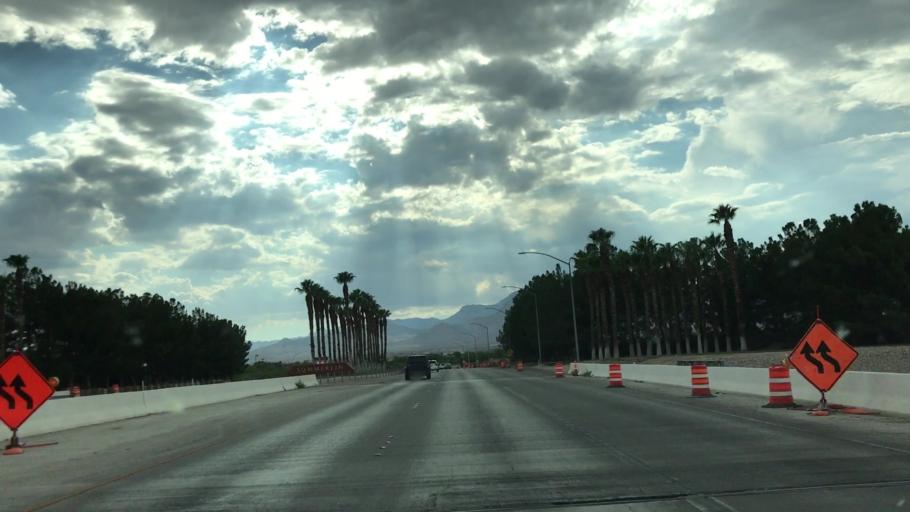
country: US
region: Nevada
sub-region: Clark County
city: Summerlin South
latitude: 36.1780
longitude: -115.2871
